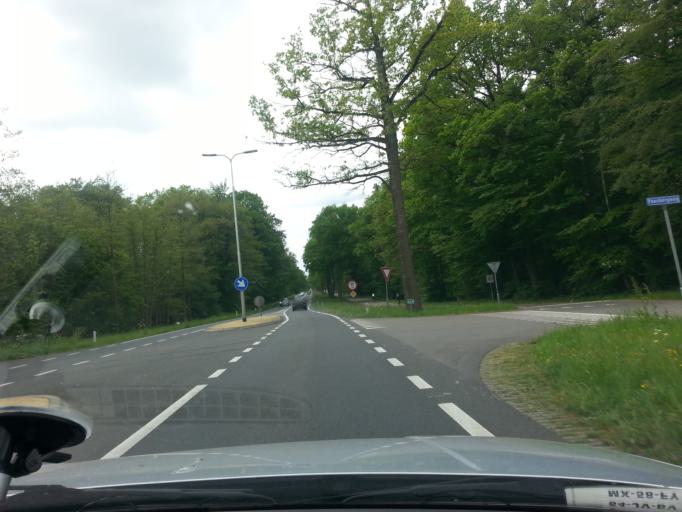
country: NL
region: Overijssel
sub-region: Gemeente Oldenzaal
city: Oldenzaal
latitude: 52.3358
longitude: 6.9572
